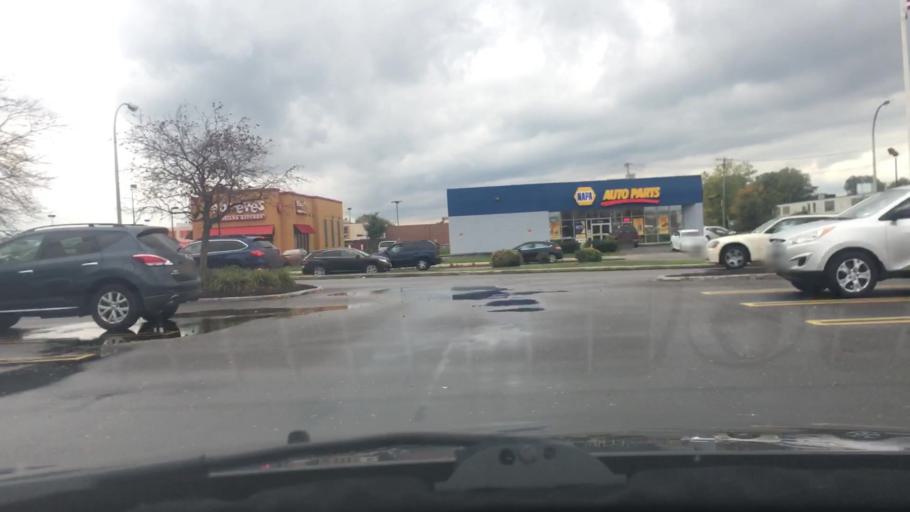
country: US
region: New York
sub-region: Erie County
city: Kenmore
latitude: 42.9545
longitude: -78.8777
